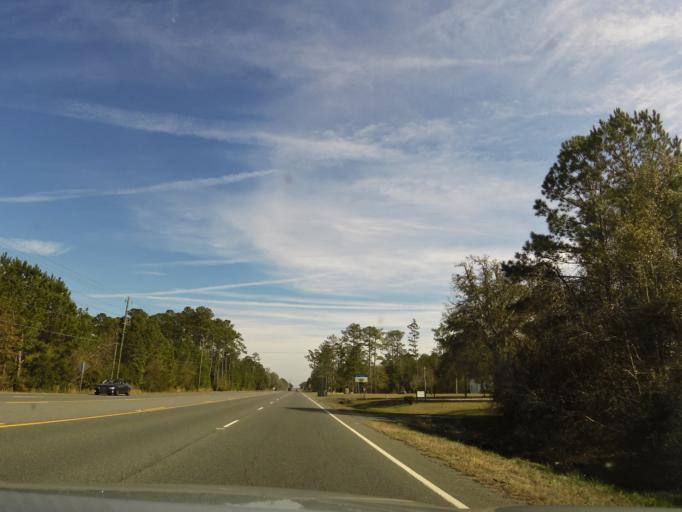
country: US
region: Georgia
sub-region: Brantley County
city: Nahunta
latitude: 31.2296
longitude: -81.7859
